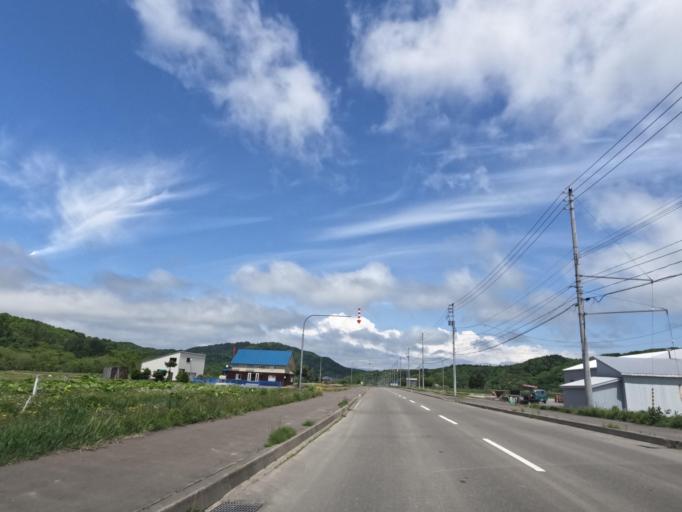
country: JP
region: Hokkaido
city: Tobetsu
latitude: 43.2995
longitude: 141.5476
